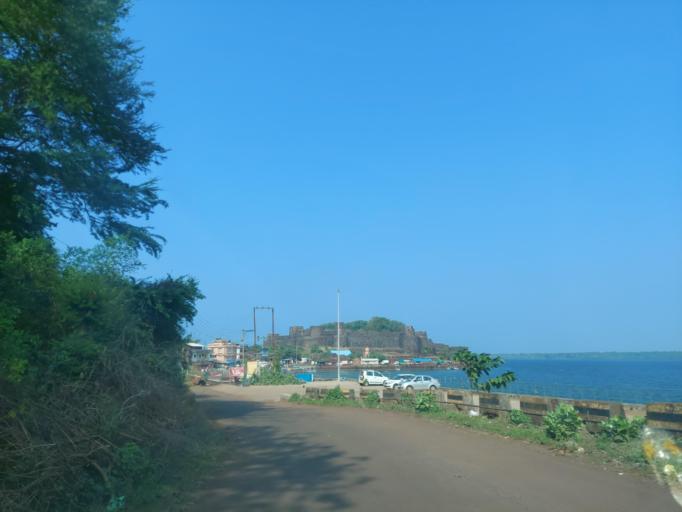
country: IN
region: Maharashtra
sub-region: Ratnagiri
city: Rajapur
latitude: 16.5566
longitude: 73.3370
